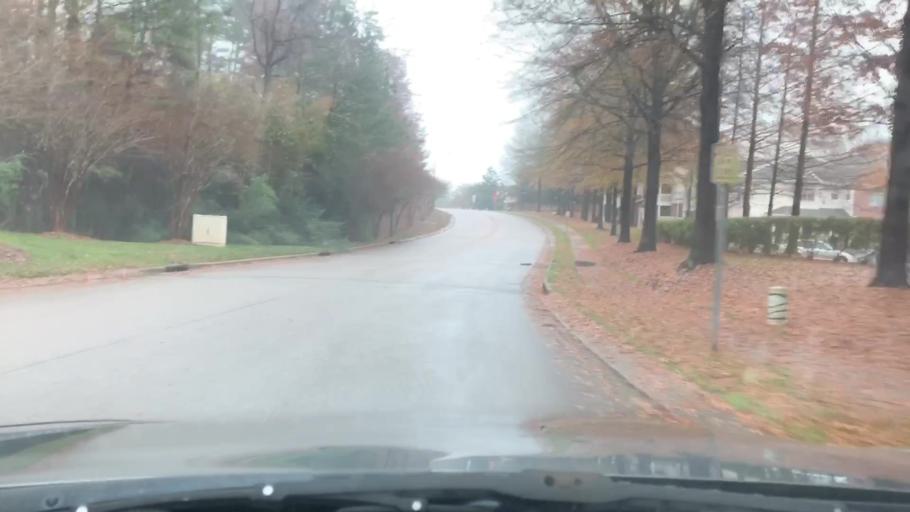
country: US
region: North Carolina
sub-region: Wake County
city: West Raleigh
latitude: 35.8473
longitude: -78.6716
